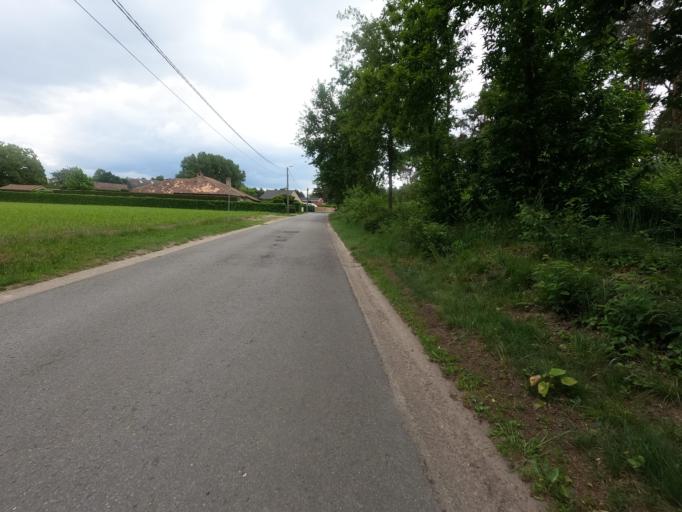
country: BE
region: Flanders
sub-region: Provincie Vlaams-Brabant
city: Tremelo
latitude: 51.0060
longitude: 4.7355
